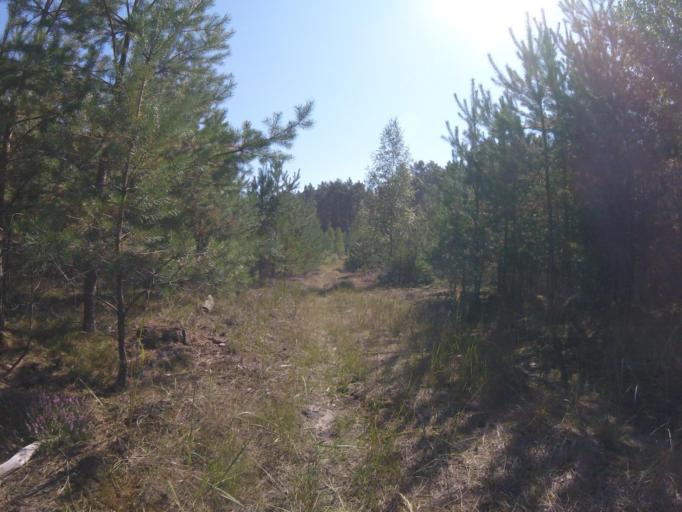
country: DE
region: Brandenburg
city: Bestensee
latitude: 52.2693
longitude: 13.6809
